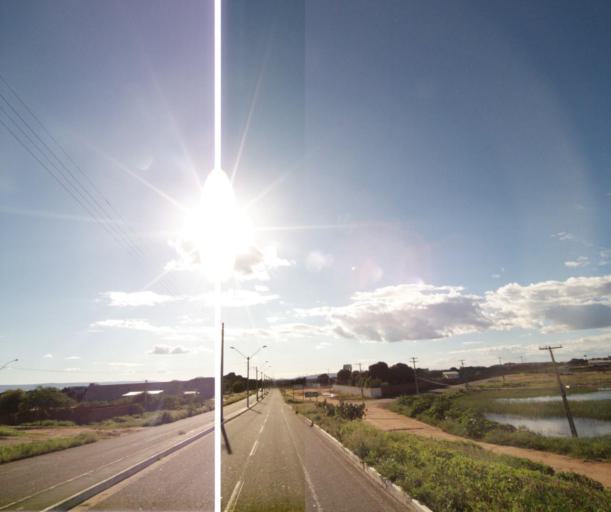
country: BR
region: Bahia
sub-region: Guanambi
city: Guanambi
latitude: -14.2110
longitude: -42.7948
